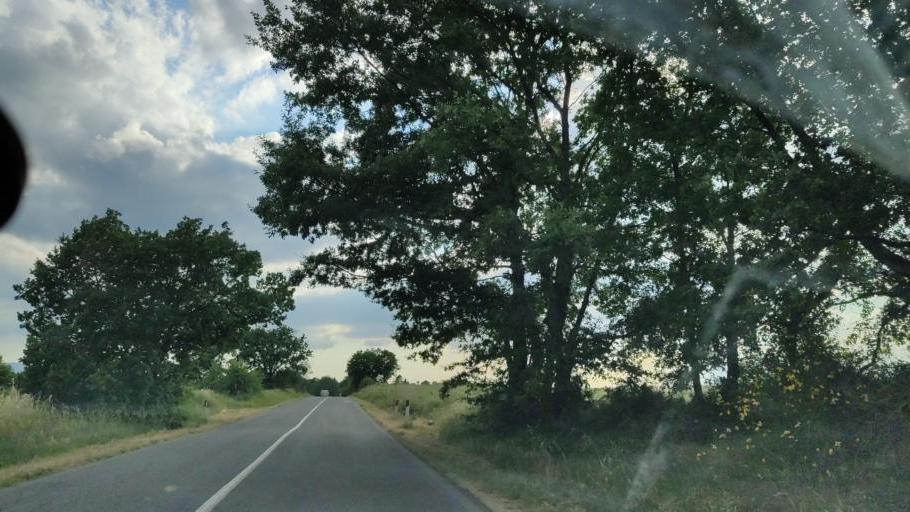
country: IT
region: Umbria
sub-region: Provincia di Terni
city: Penna in Teverina
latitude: 42.5158
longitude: 12.3646
